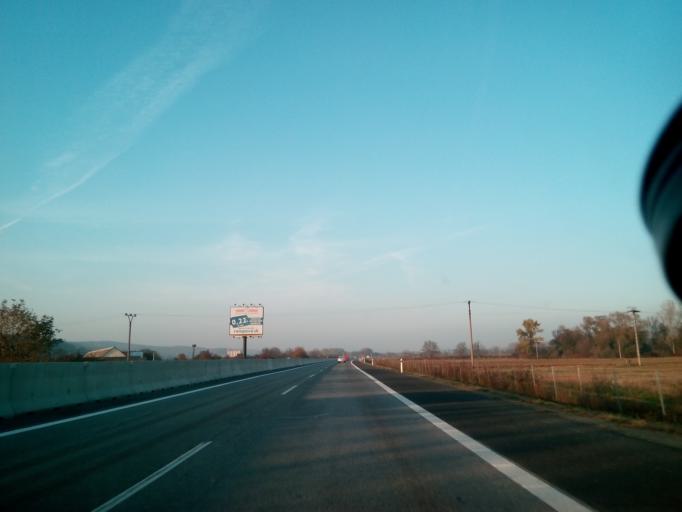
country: SK
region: Presovsky
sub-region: Okres Presov
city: Presov
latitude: 48.8970
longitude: 21.2488
